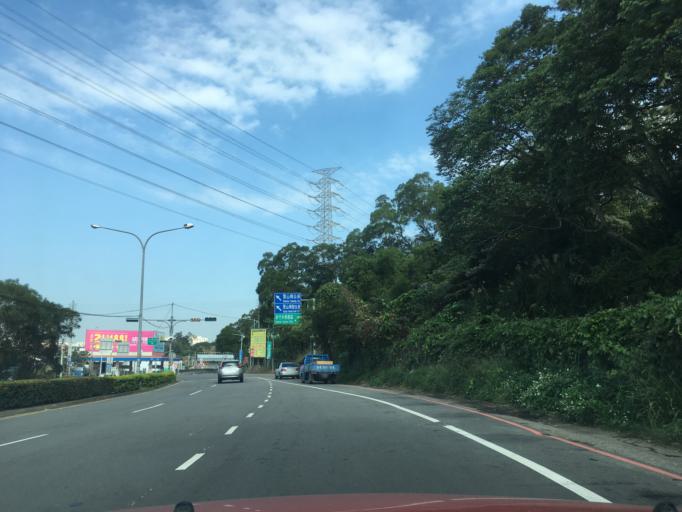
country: TW
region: Taiwan
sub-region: Hsinchu
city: Hsinchu
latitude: 24.7583
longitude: 121.0063
